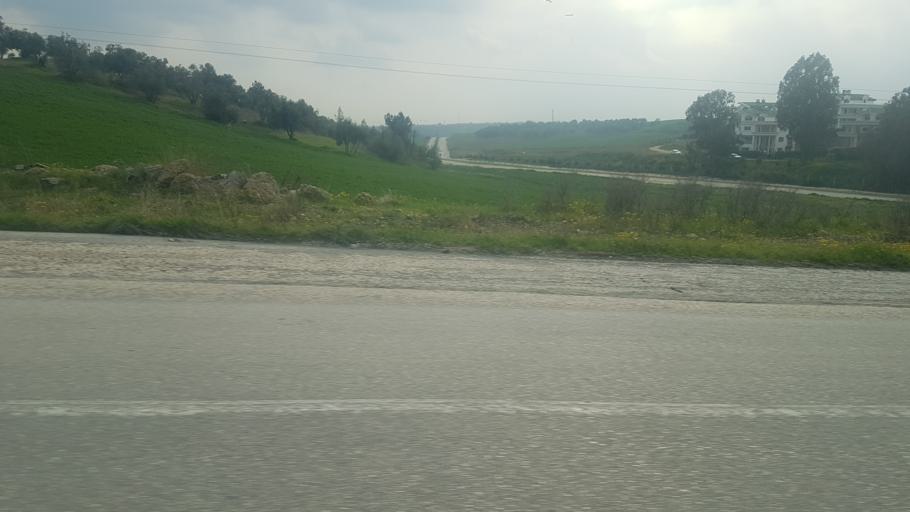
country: TR
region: Adana
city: Seyhan
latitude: 37.0463
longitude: 35.1801
